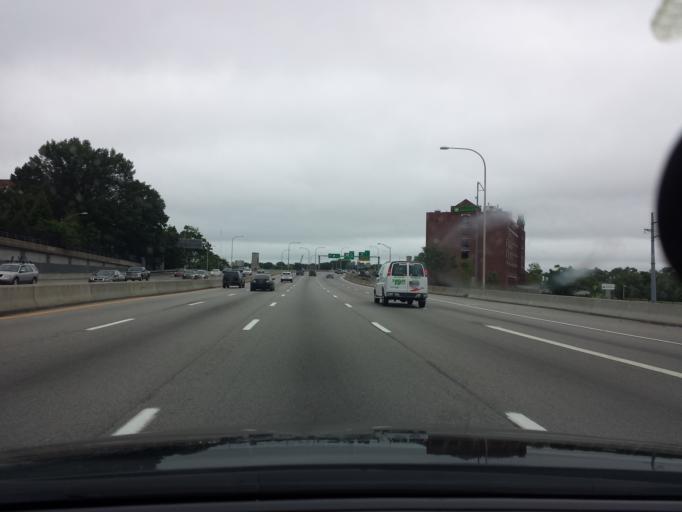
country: US
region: Rhode Island
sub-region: Providence County
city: Providence
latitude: 41.8187
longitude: -71.3933
